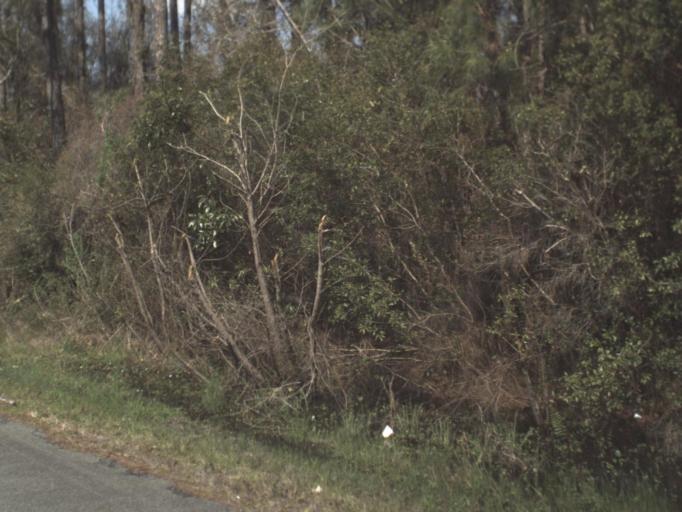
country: US
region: Florida
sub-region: Franklin County
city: Carrabelle
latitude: 29.9756
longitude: -84.4994
